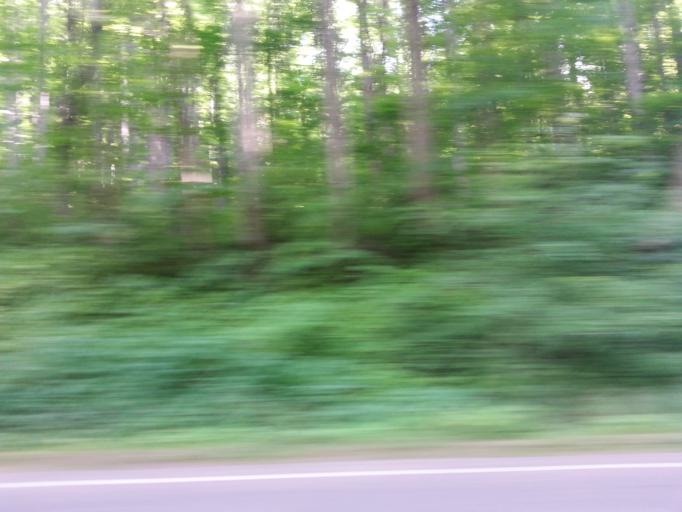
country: US
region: Tennessee
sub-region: Sevier County
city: Gatlinburg
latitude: 35.6623
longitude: -83.5251
